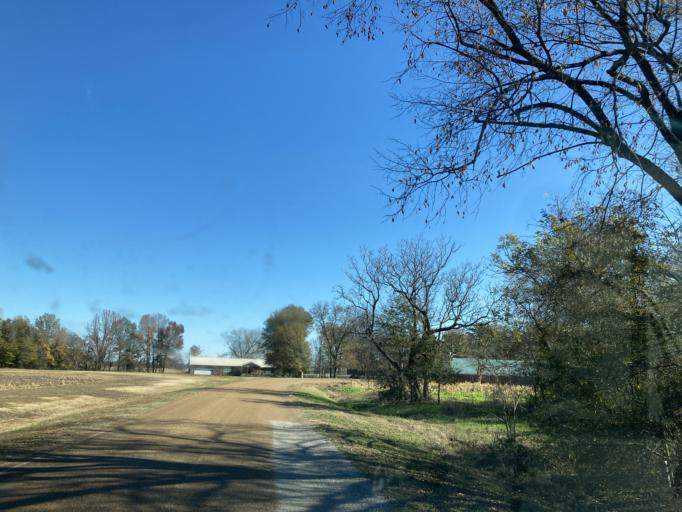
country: US
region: Mississippi
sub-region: Yazoo County
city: Yazoo City
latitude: 32.9232
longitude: -90.4921
